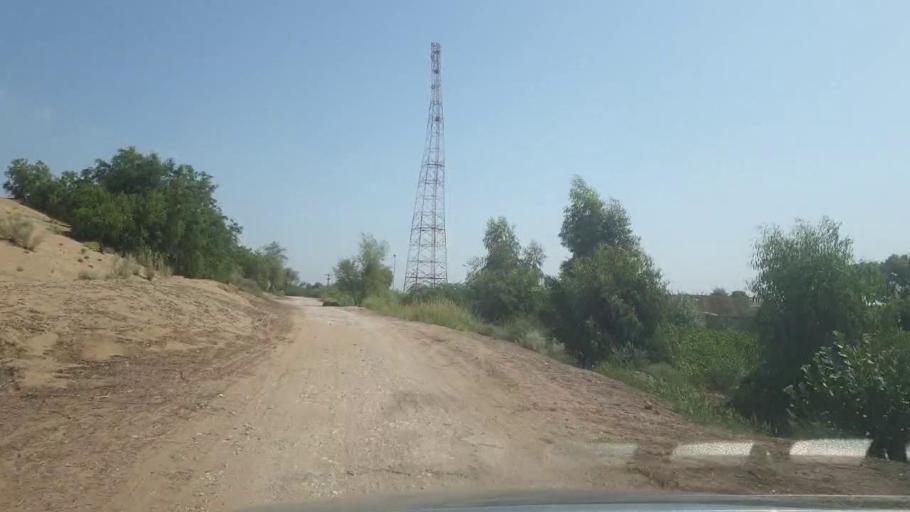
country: PK
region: Sindh
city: Khairpur
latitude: 27.4005
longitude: 69.0800
